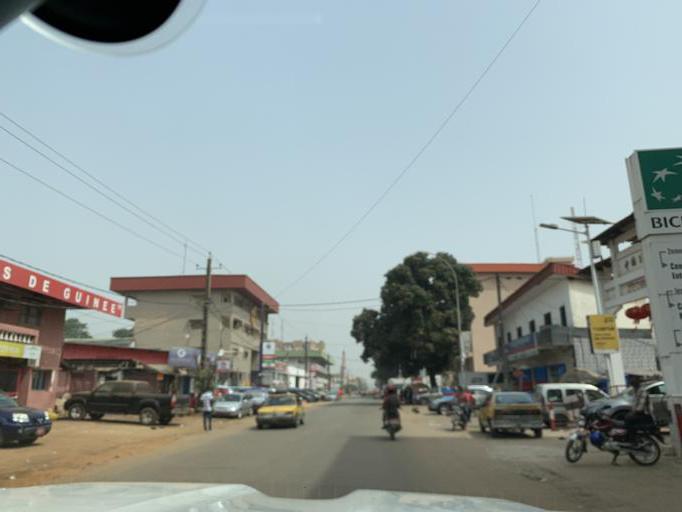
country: GN
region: Conakry
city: Camayenne
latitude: 9.5291
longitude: -13.6828
